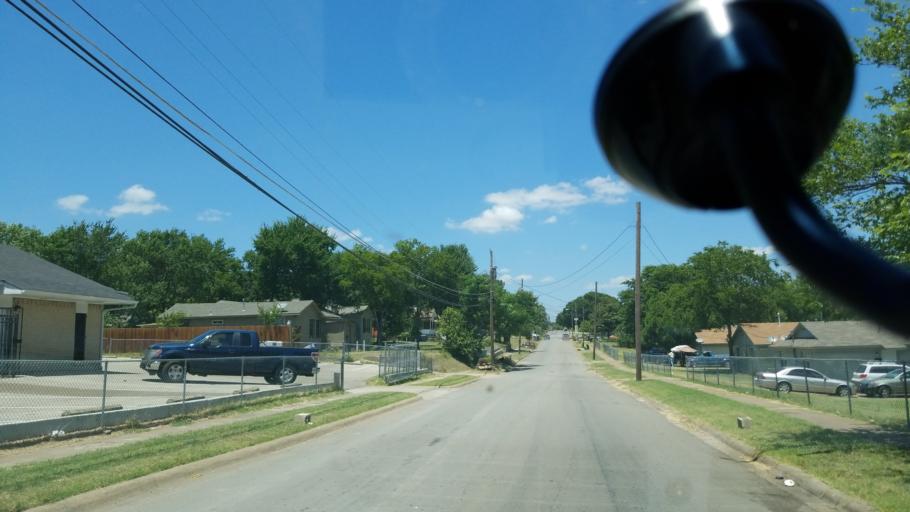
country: US
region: Texas
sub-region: Dallas County
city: Cockrell Hill
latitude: 32.6914
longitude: -96.8118
